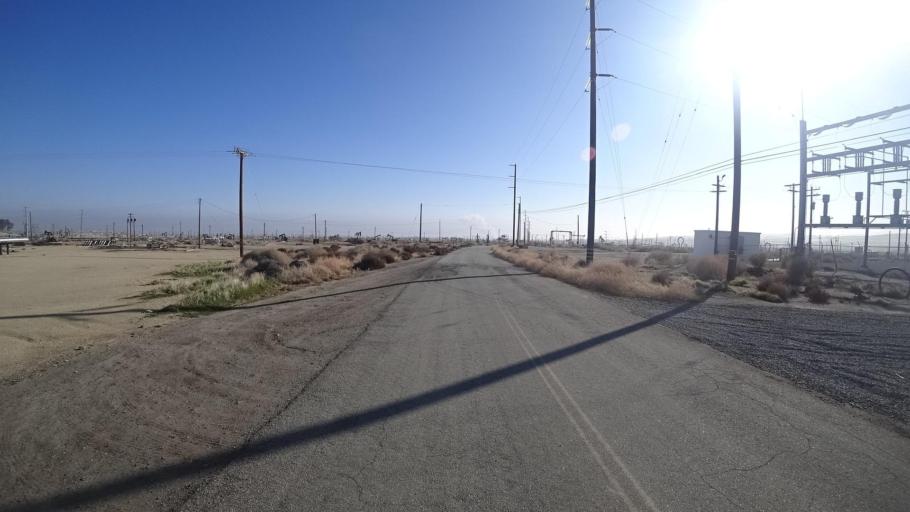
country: US
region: California
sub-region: Kern County
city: Taft Heights
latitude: 35.2263
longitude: -119.6276
